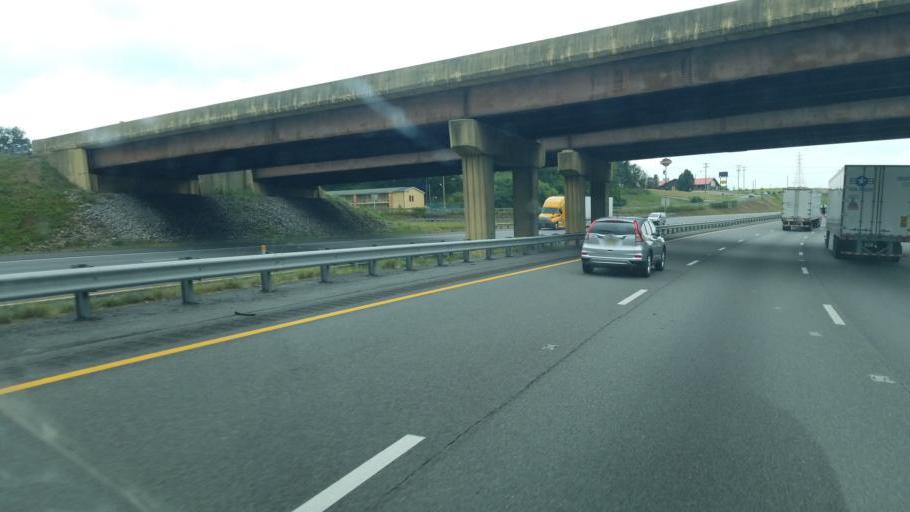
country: US
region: Virginia
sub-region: Wythe County
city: Wytheville
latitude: 36.9487
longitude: -81.0529
